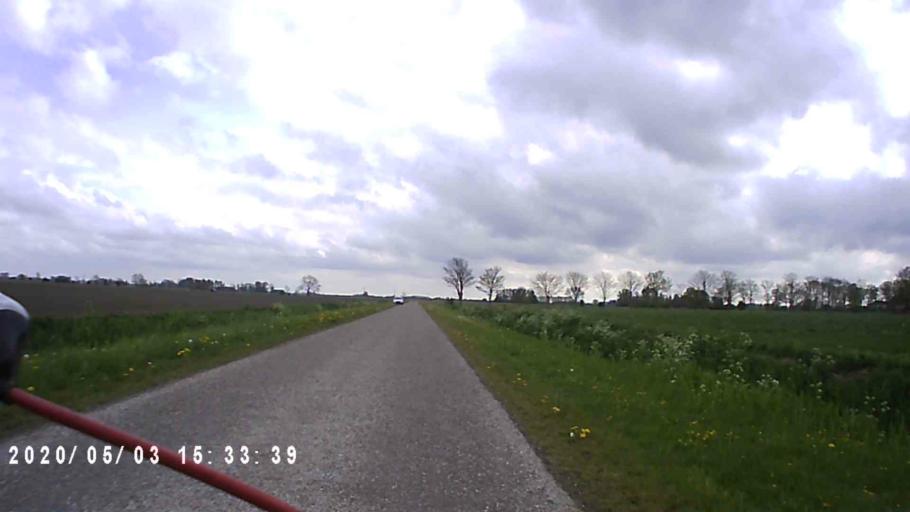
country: NL
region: Groningen
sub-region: Gemeente Winsum
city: Winsum
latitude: 53.3342
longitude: 6.4735
